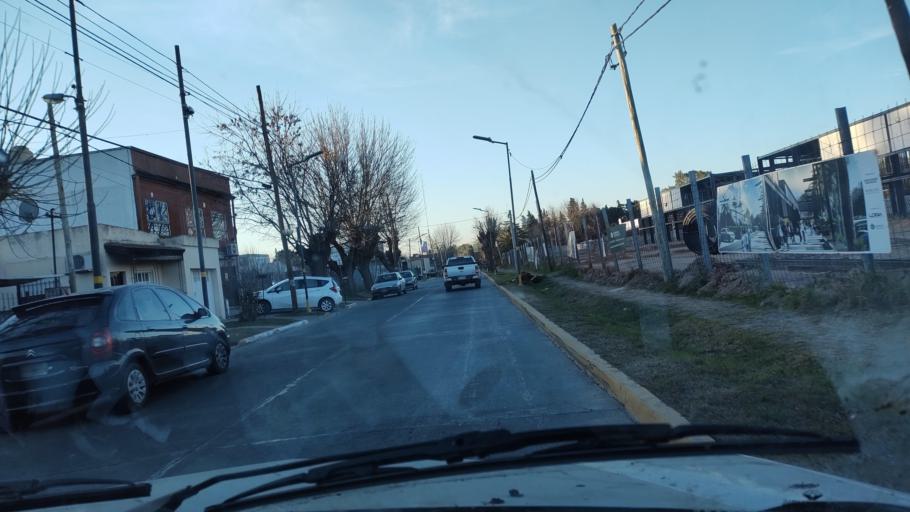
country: AR
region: Buenos Aires
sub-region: Partido de La Plata
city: La Plata
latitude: -34.9037
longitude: -58.0442
